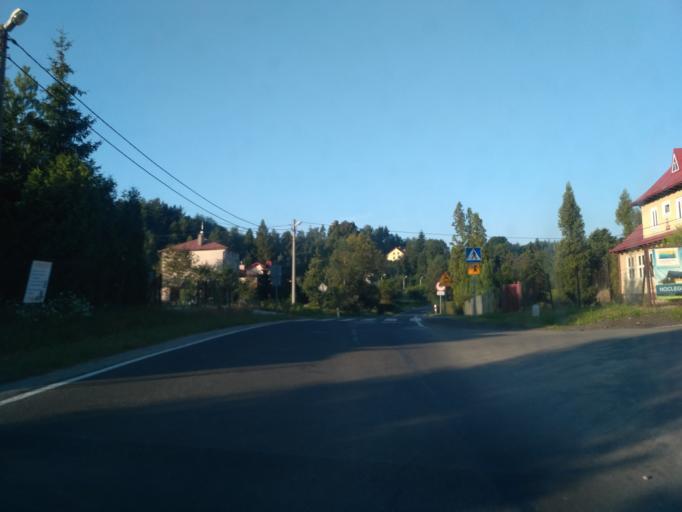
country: PL
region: Subcarpathian Voivodeship
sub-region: Powiat krosnienski
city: Korczyna
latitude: 49.7458
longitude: 21.8029
